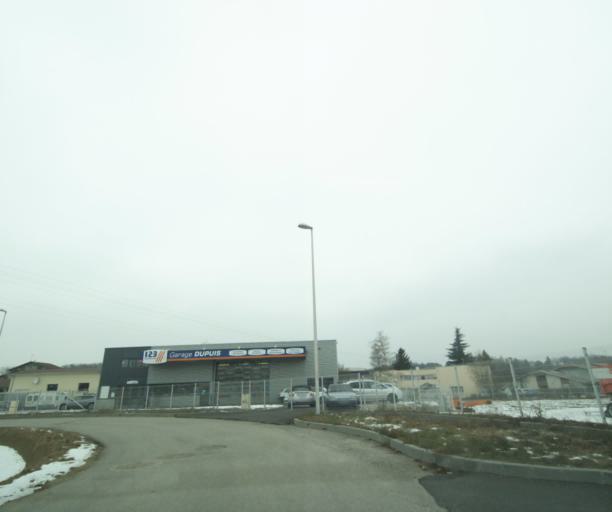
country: FR
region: Rhone-Alpes
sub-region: Departement de la Haute-Savoie
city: Reignier-Esery
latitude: 46.1330
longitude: 6.3016
